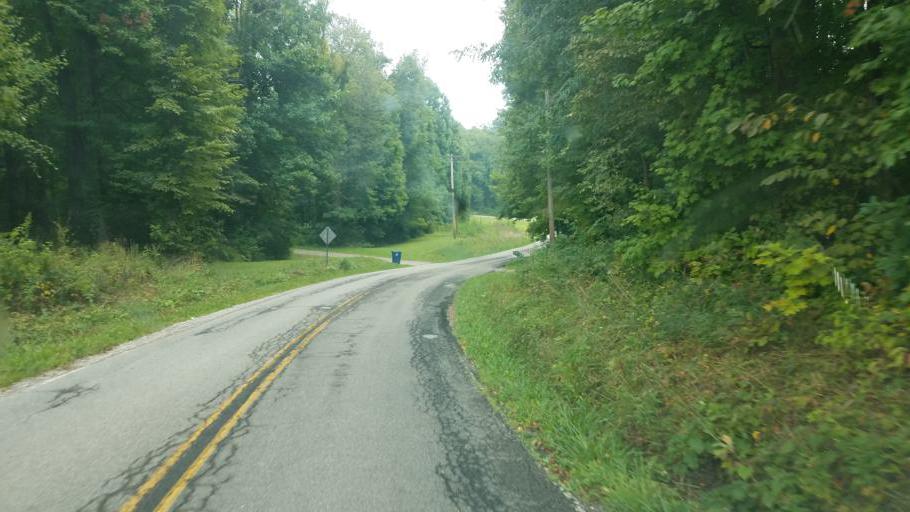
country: US
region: Ohio
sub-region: Licking County
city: Utica
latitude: 40.1958
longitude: -82.4793
